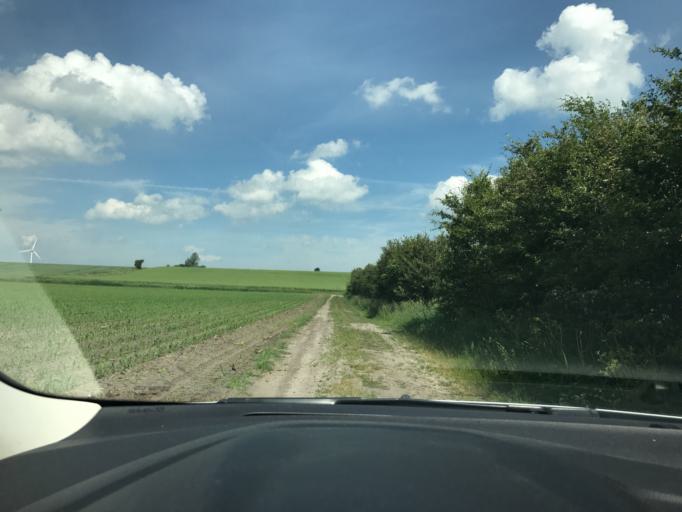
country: DE
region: Schleswig-Holstein
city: Ellhoft
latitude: 54.9271
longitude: 8.9522
